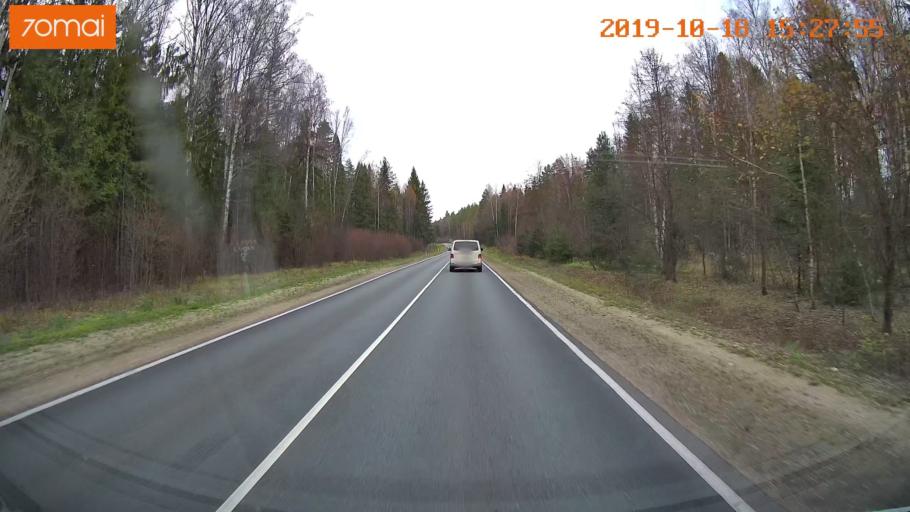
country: RU
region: Vladimir
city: Anopino
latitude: 55.7596
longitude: 40.6728
